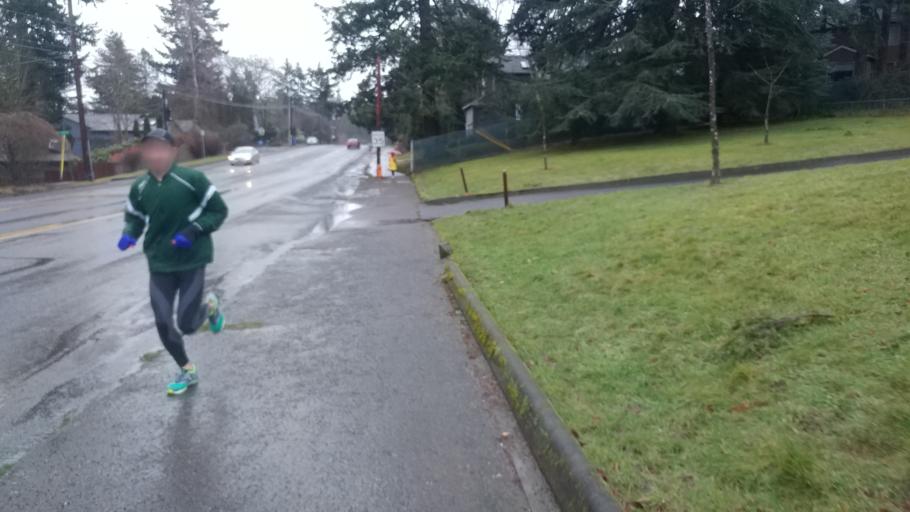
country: US
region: Oregon
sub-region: Washington County
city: Metzger
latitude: 45.4479
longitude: -122.7129
